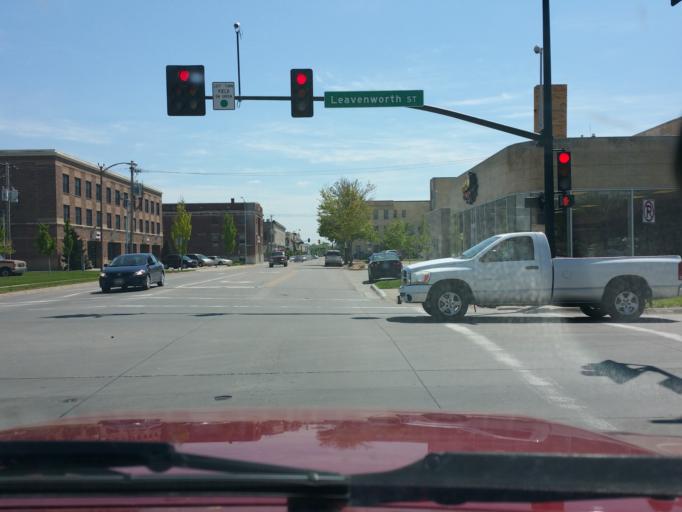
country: US
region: Kansas
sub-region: Riley County
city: Manhattan
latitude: 39.1815
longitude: -96.5618
